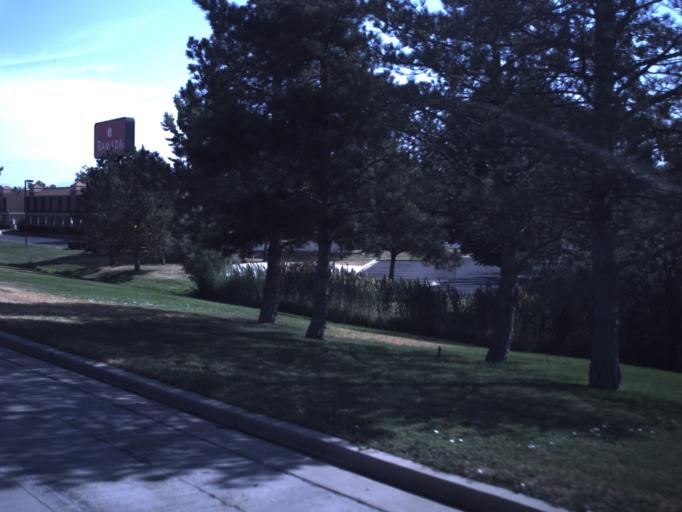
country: US
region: Utah
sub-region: Salt Lake County
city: West Valley City
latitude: 40.7737
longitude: -112.0250
